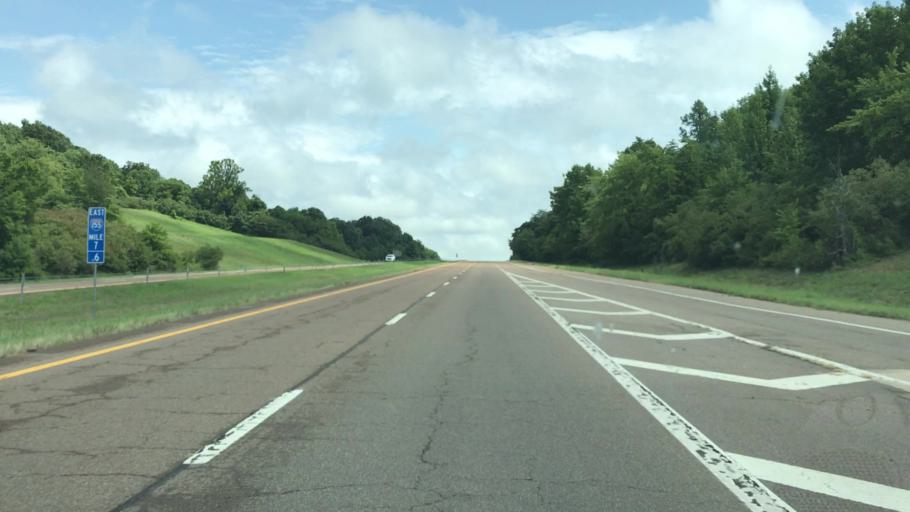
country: US
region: Tennessee
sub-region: Dyer County
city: Dyersburg
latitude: 36.0749
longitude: -89.4922
